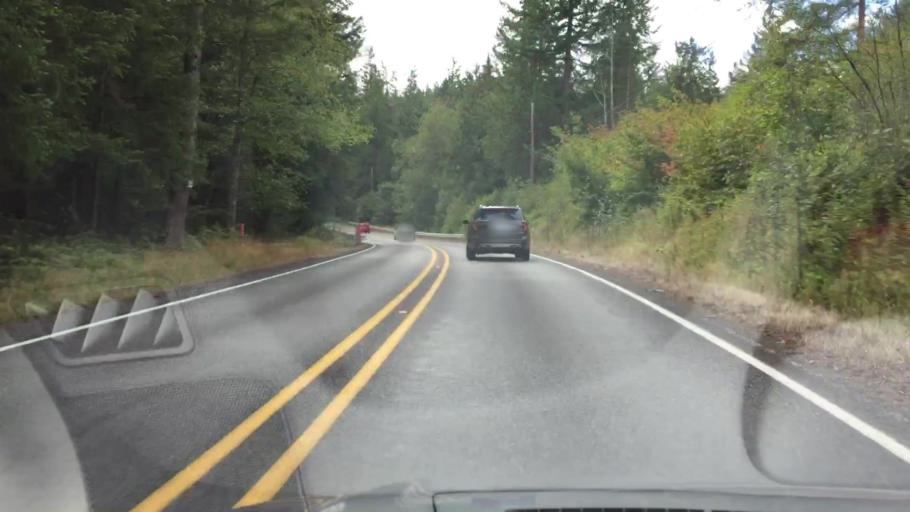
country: US
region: Washington
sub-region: Pierce County
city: Eatonville
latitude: 46.8211
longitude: -122.2645
